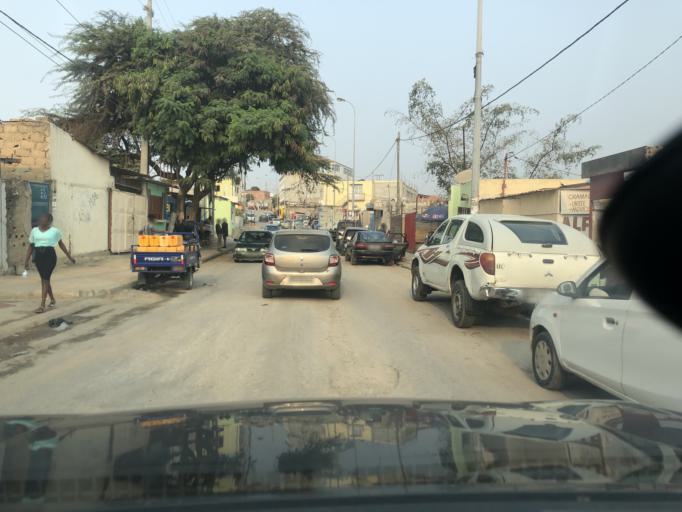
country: AO
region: Luanda
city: Luanda
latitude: -8.8802
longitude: 13.1917
